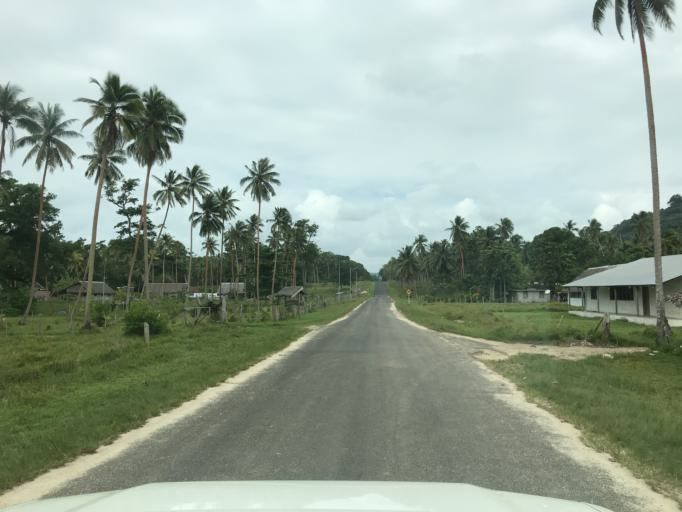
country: VU
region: Sanma
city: Port-Olry
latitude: -15.0453
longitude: 167.0720
